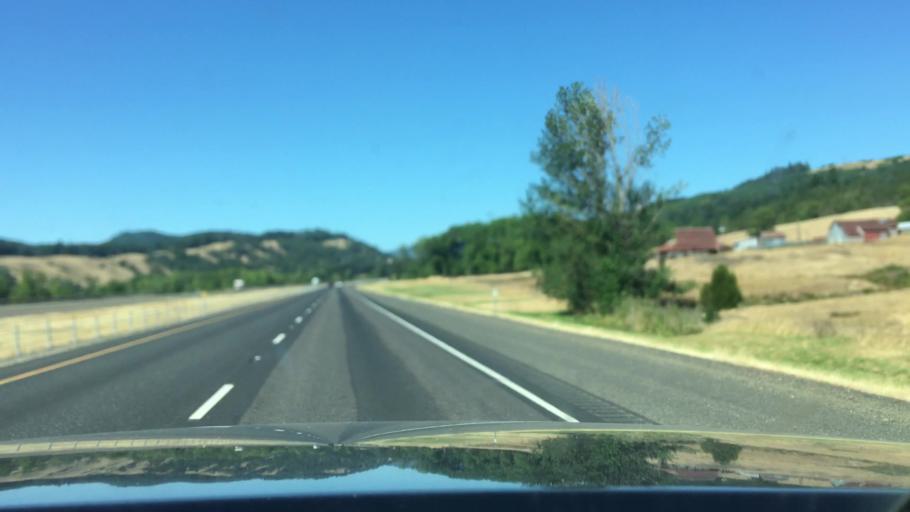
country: US
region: Oregon
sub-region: Douglas County
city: Yoncalla
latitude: 43.5860
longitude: -123.2544
